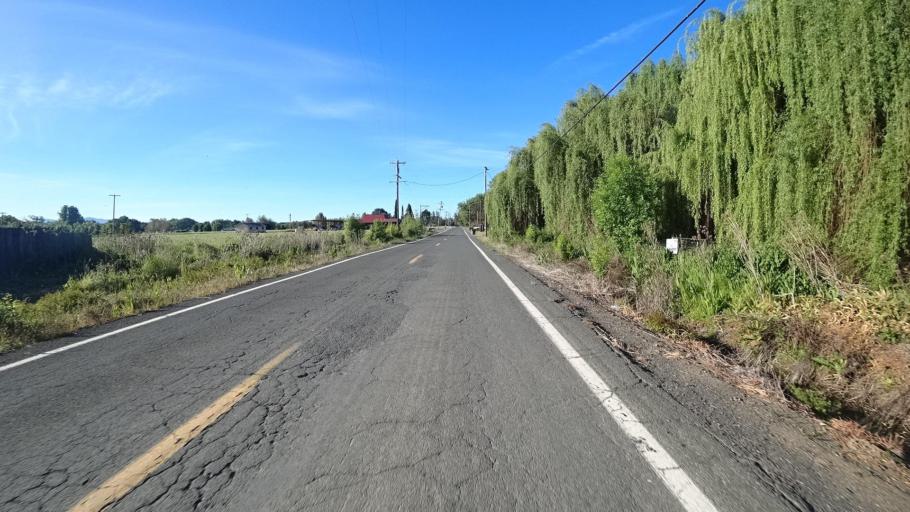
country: US
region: California
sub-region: Lake County
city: North Lakeport
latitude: 39.0830
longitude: -122.9498
